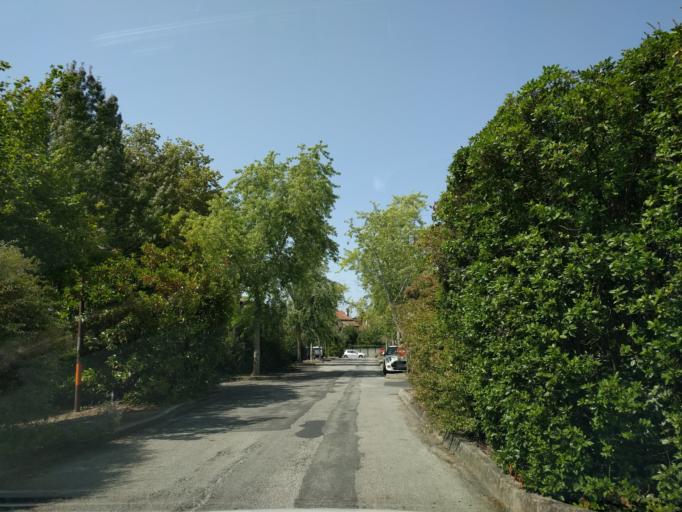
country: FR
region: Midi-Pyrenees
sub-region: Departement du Tarn
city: Castres
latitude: 43.6019
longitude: 2.2478
